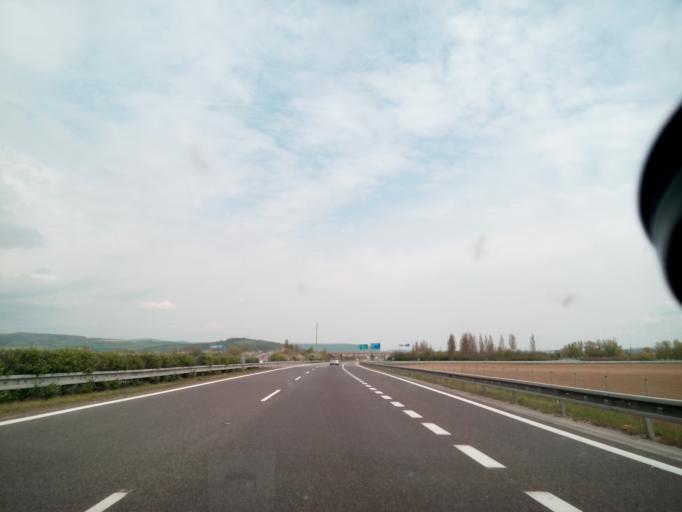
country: SK
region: Trenciansky
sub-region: Okres Trencin
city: Trencin
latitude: 48.8564
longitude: 17.9533
